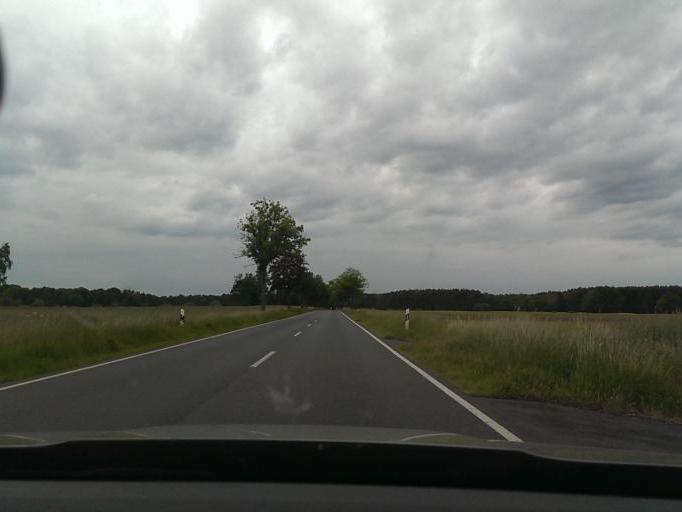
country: DE
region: Lower Saxony
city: Winsen (Aller)
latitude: 52.6815
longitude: 9.8830
